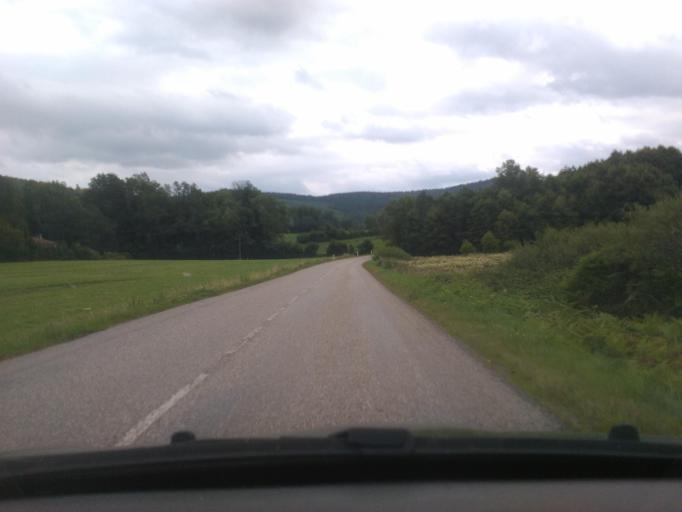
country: FR
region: Lorraine
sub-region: Departement des Vosges
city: Granges-sur-Vologne
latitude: 48.1743
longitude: 6.7699
